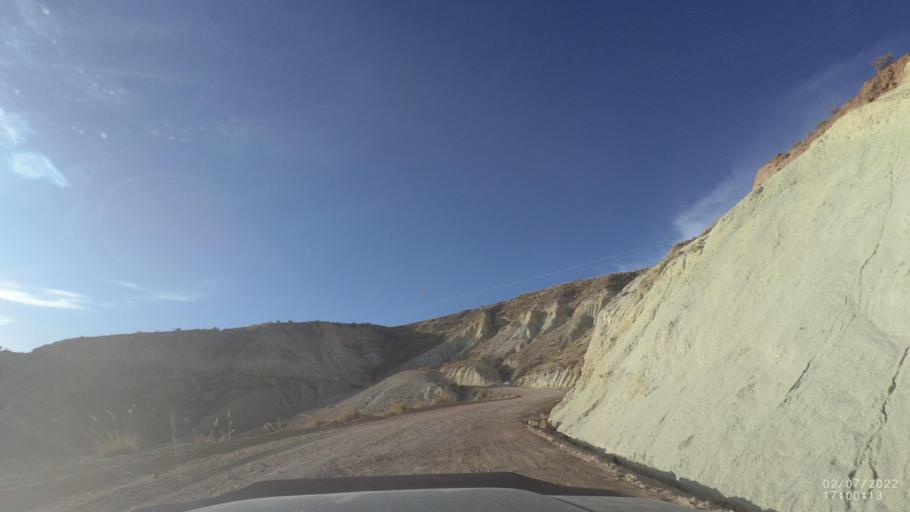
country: BO
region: Cochabamba
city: Irpa Irpa
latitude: -17.9384
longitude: -66.5537
